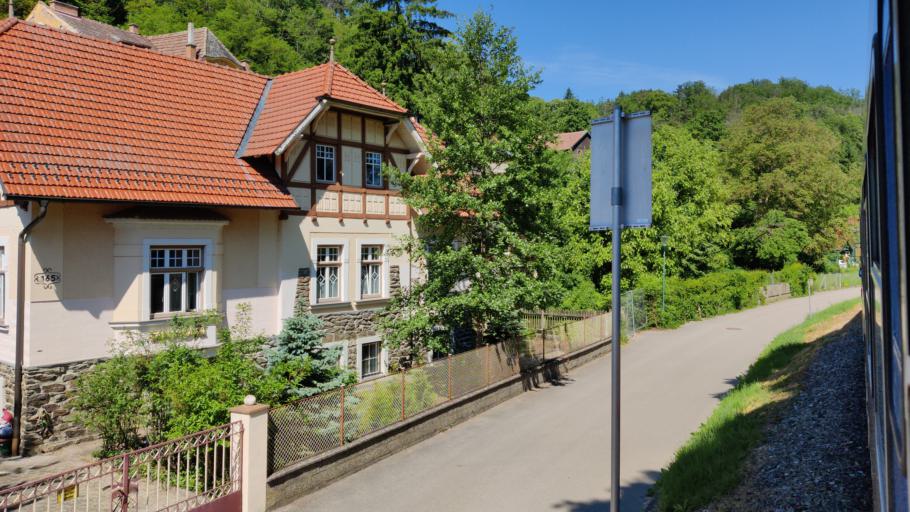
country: AT
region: Lower Austria
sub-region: Politischer Bezirk Horn
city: Gars am Kamp
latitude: 48.5949
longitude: 15.6561
